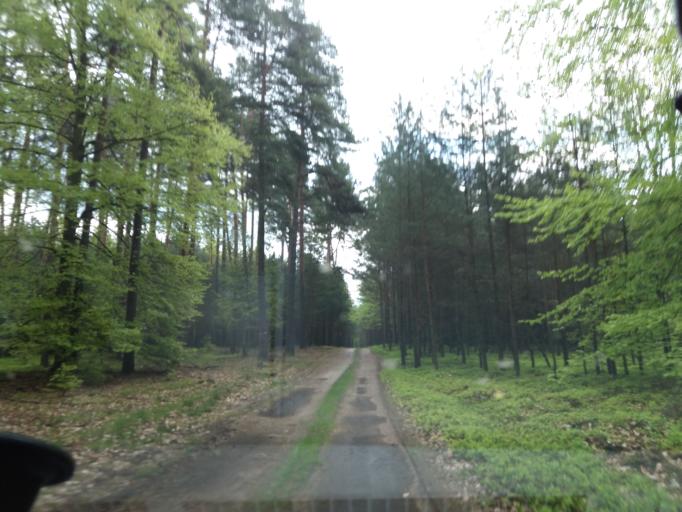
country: PL
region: West Pomeranian Voivodeship
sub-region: Powiat choszczenski
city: Drawno
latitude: 53.1107
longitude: 15.8761
